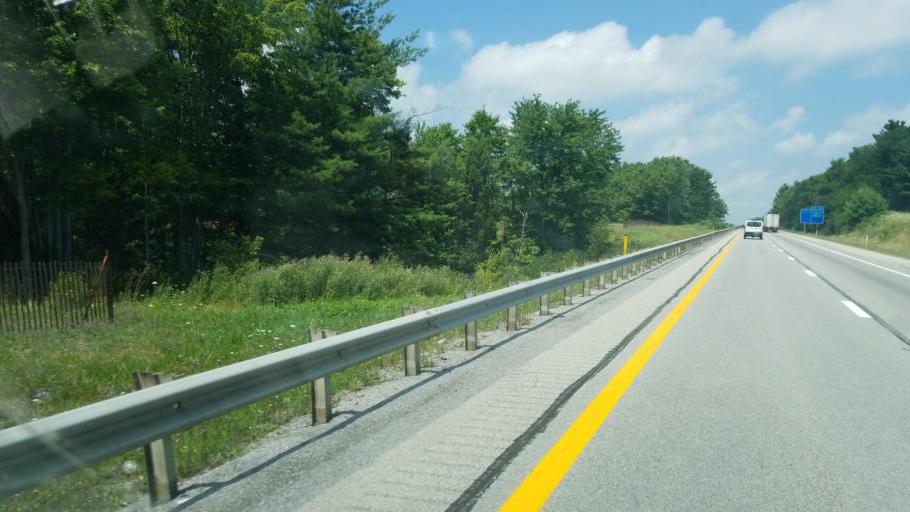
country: US
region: West Virginia
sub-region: Mercer County
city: Athens
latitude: 37.4078
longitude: -81.0608
